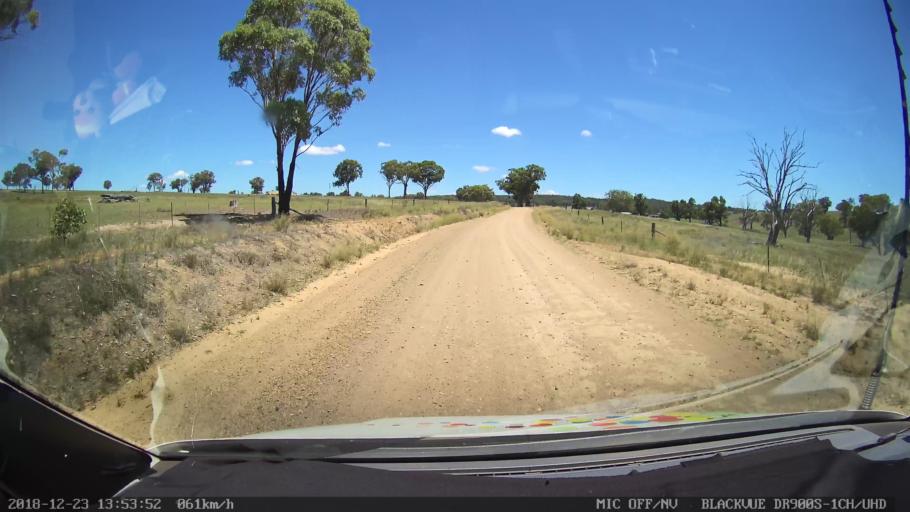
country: AU
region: New South Wales
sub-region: Tamworth Municipality
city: Manilla
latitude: -30.5558
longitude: 151.0921
